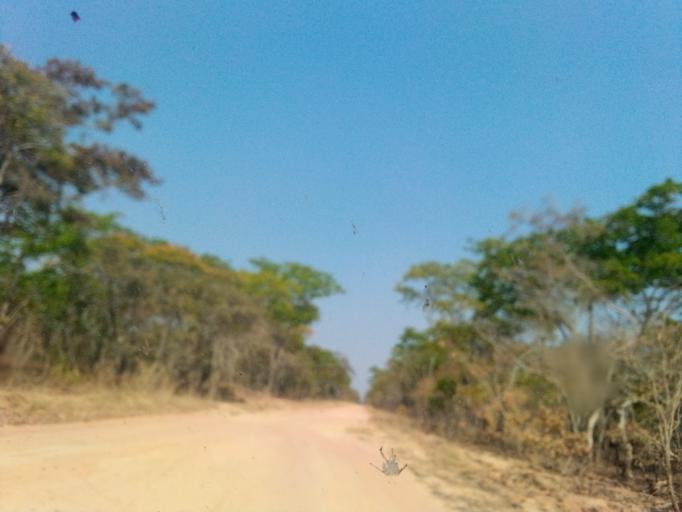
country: ZM
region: Northern
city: Mpika
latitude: -12.2419
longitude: 30.8532
